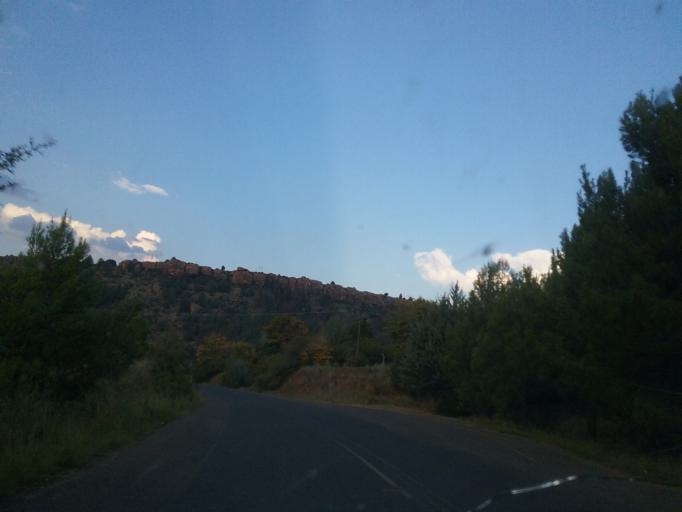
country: LS
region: Quthing
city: Quthing
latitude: -30.4034
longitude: 27.6782
